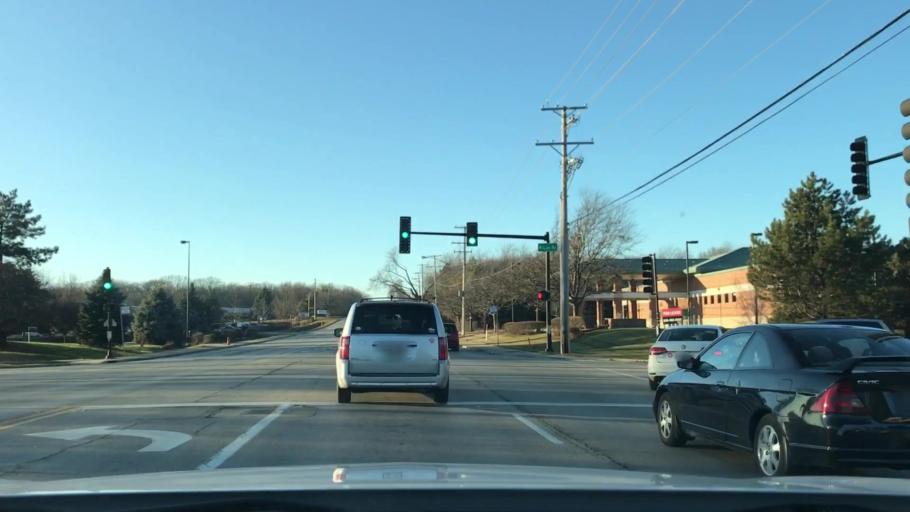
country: US
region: Illinois
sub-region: Kane County
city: Sleepy Hollow
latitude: 42.0609
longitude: -88.3269
